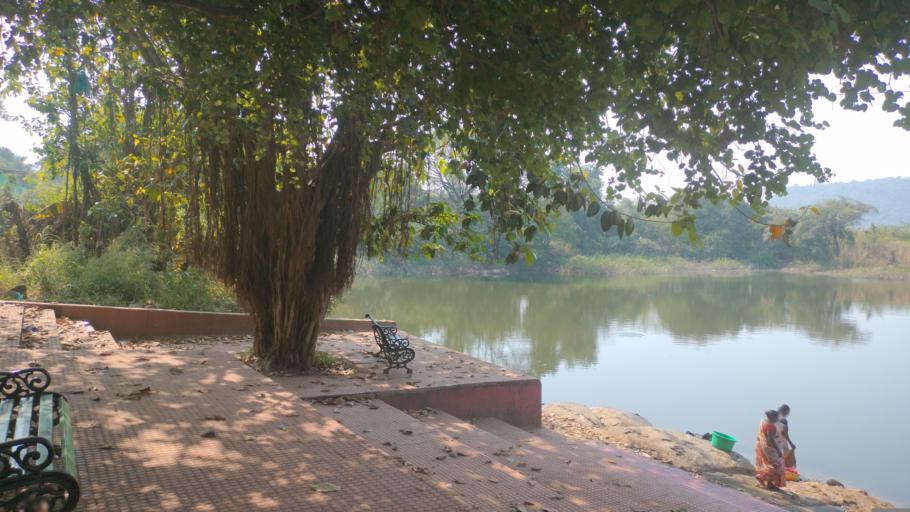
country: IN
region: Maharashtra
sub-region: Thane
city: Bhayandar
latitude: 19.3588
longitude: 72.9118
